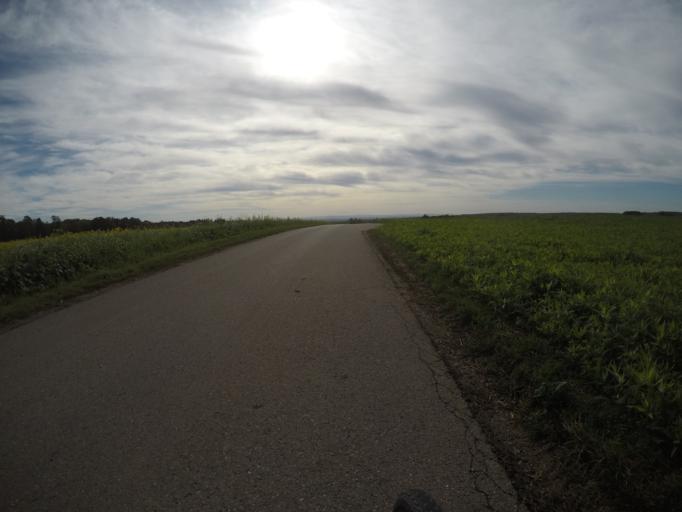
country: DE
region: Baden-Wuerttemberg
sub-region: Regierungsbezirk Stuttgart
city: Deckenpfronn
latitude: 48.6491
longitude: 8.8418
